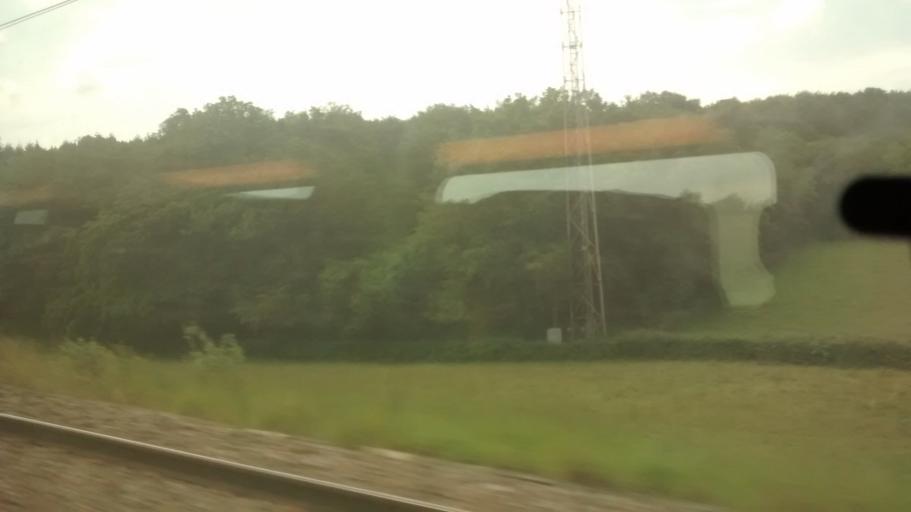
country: FR
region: Bourgogne
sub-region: Departement de Saone-et-Loire
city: Saint-Gengoux-le-National
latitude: 46.5618
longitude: 4.6273
